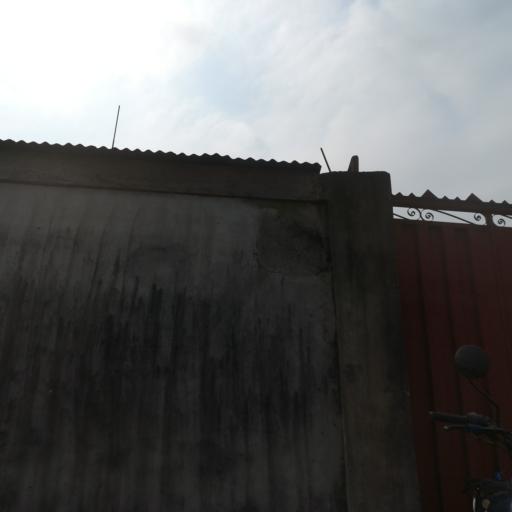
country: NG
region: Rivers
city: Port Harcourt
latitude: 4.8406
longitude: 7.0652
